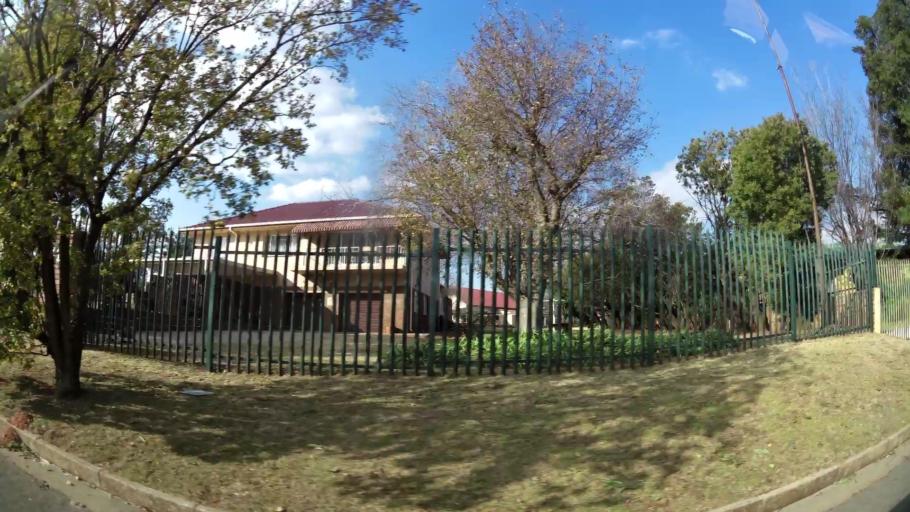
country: ZA
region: Gauteng
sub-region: West Rand District Municipality
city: Krugersdorp
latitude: -26.0934
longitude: 27.7615
